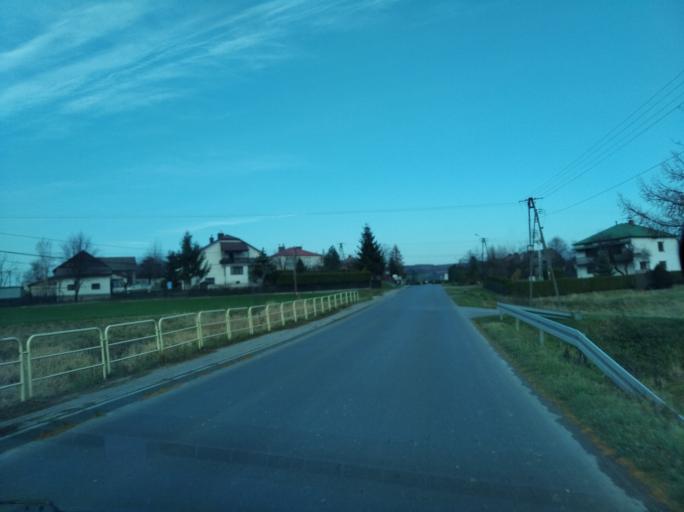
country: PL
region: Subcarpathian Voivodeship
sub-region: Powiat ropczycko-sedziszowski
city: Iwierzyce
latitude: 50.0246
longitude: 21.7555
